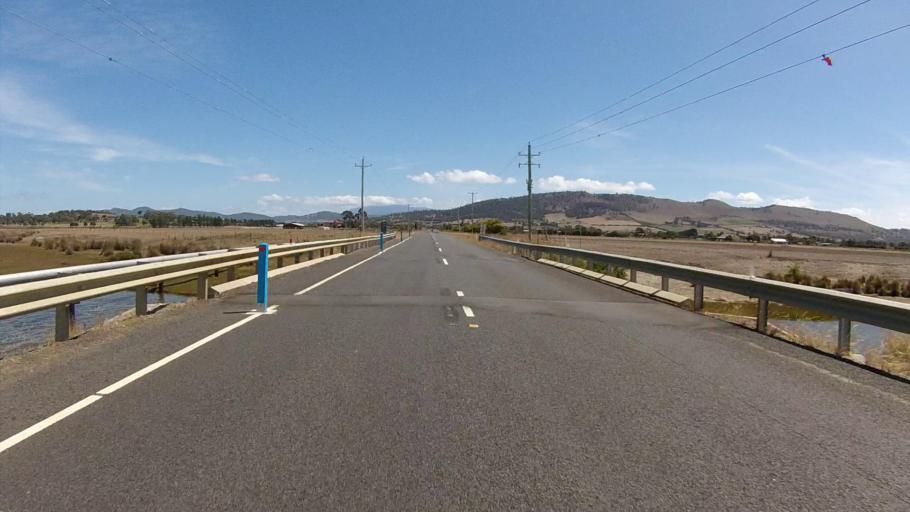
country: AU
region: Tasmania
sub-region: Sorell
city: Sorell
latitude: -42.7749
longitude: 147.5352
